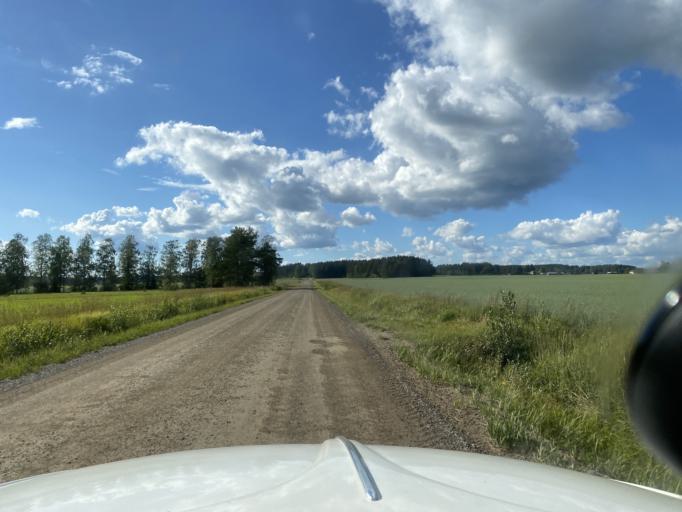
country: FI
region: Pirkanmaa
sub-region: Lounais-Pirkanmaa
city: Punkalaidun
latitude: 61.1341
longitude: 23.2292
